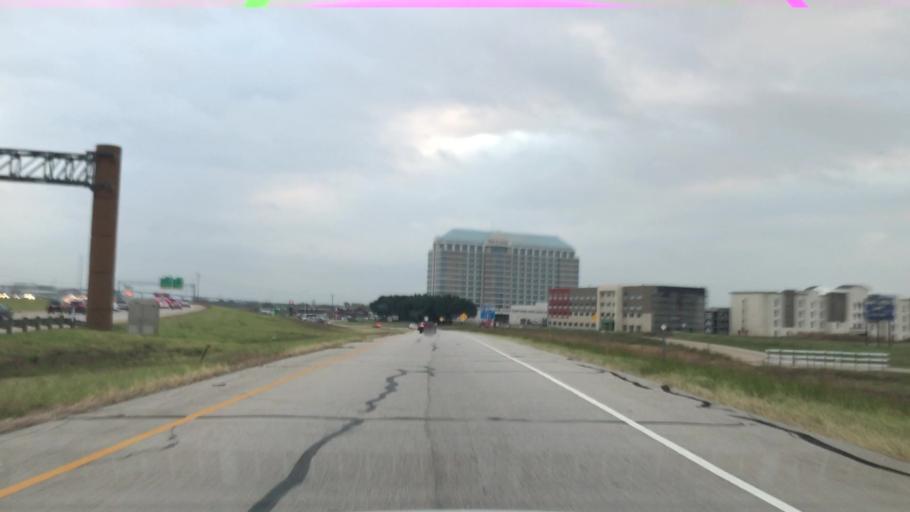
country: US
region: Texas
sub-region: Dallas County
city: Farmers Branch
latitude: 32.9074
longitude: -96.9254
